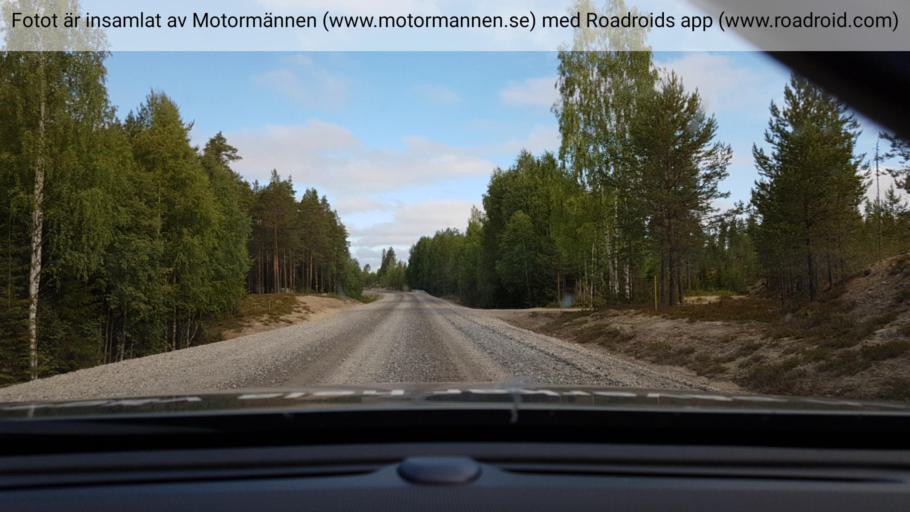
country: SE
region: Vaesterbotten
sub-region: Norsjo Kommun
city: Norsjoe
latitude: 64.6700
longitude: 19.2612
